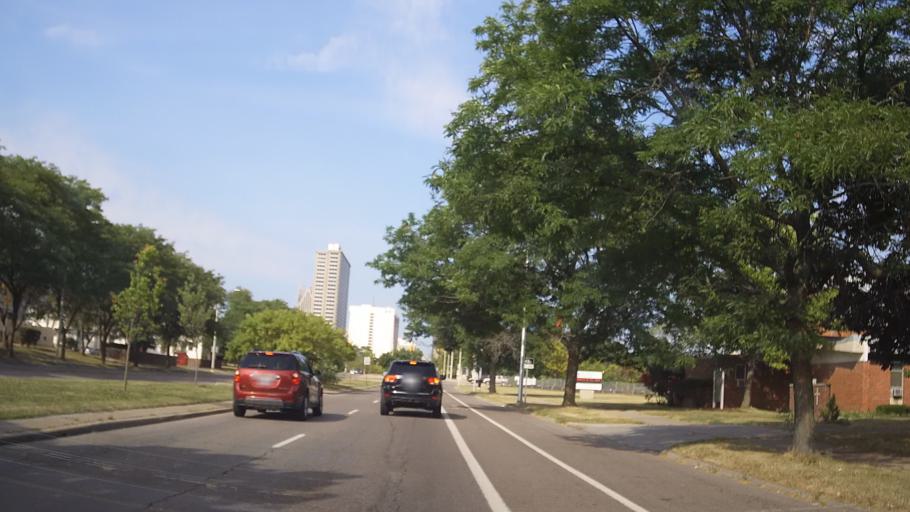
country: US
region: Michigan
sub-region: Wayne County
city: Detroit
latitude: 42.3399
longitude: -83.0283
